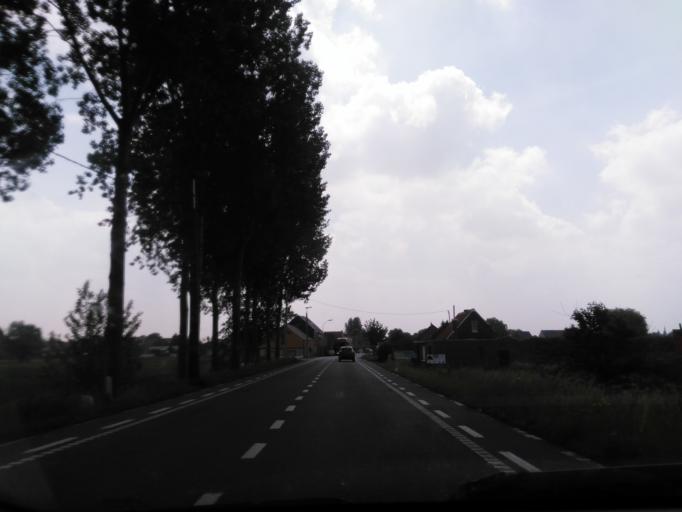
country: BE
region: Flanders
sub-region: Provincie Oost-Vlaanderen
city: Beveren
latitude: 51.2352
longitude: 4.2698
